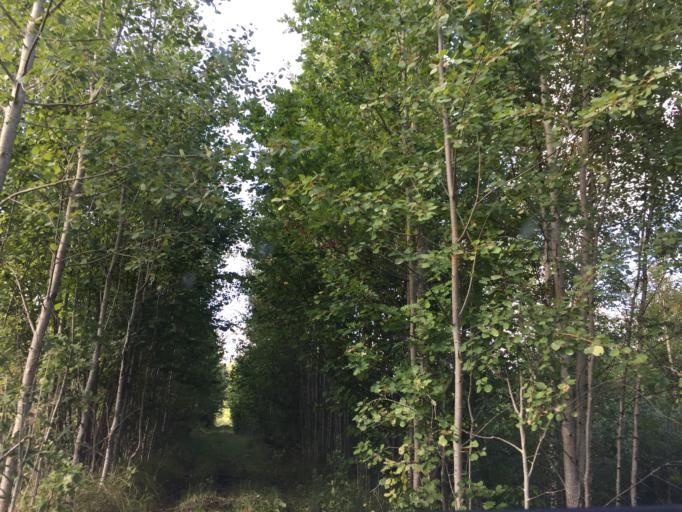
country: LV
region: Kuldigas Rajons
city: Kuldiga
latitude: 56.9792
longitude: 21.8998
